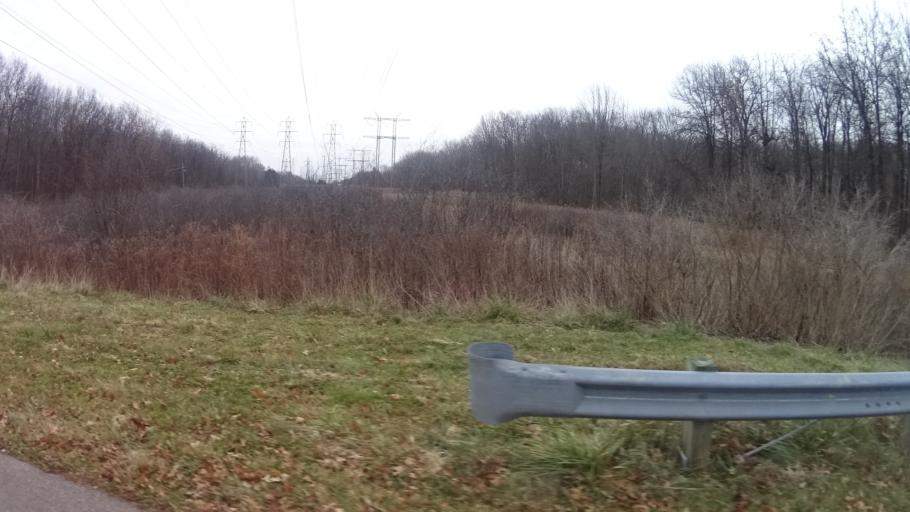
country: US
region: Ohio
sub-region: Lorain County
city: North Ridgeville
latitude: 41.3962
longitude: -81.9720
